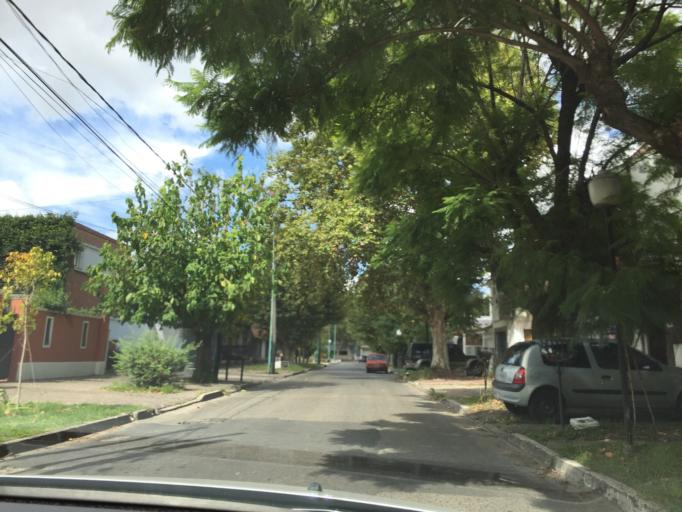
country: AR
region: Buenos Aires
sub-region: Partido de Lomas de Zamora
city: Lomas de Zamora
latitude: -34.7562
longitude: -58.3891
